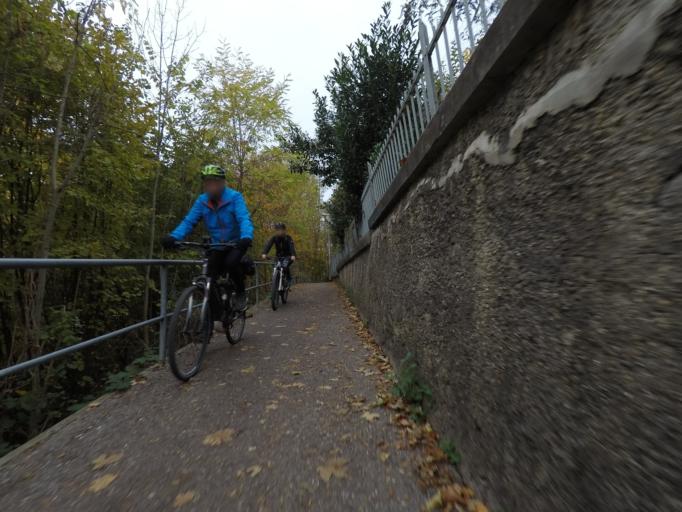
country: DE
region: Baden-Wuerttemberg
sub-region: Tuebingen Region
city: Reutlingen
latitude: 48.4973
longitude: 9.2189
